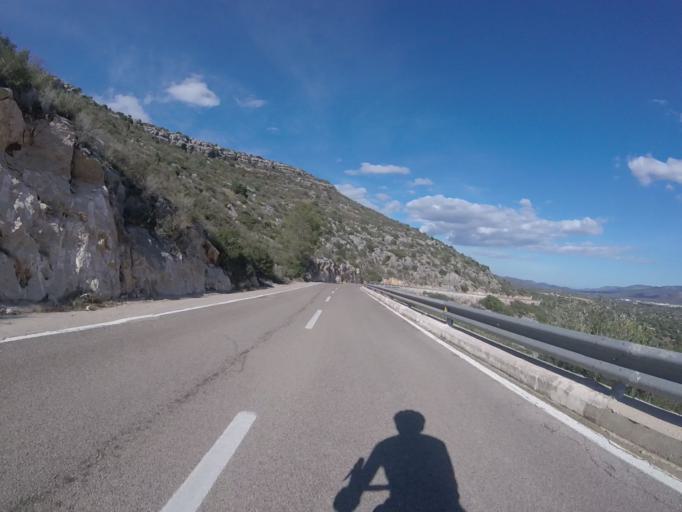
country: ES
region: Valencia
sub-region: Provincia de Castello
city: Alcala de Xivert
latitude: 40.2936
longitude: 0.1836
